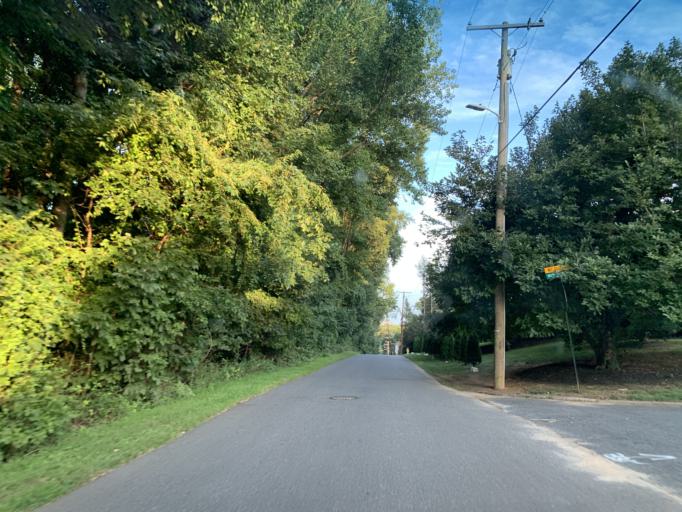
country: US
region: Maryland
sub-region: Harford County
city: Aberdeen
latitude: 39.5211
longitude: -76.1574
